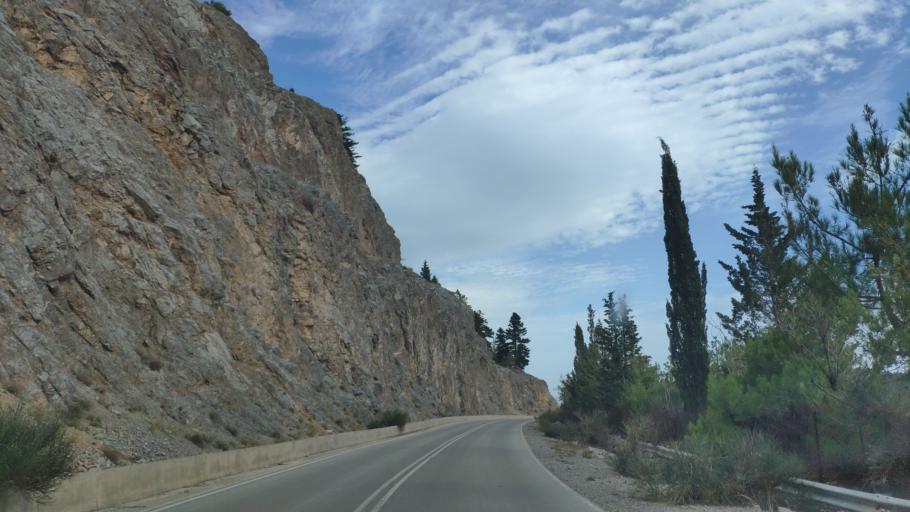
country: GR
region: Central Greece
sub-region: Nomos Fokidos
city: Amfissa
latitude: 38.6547
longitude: 22.3813
